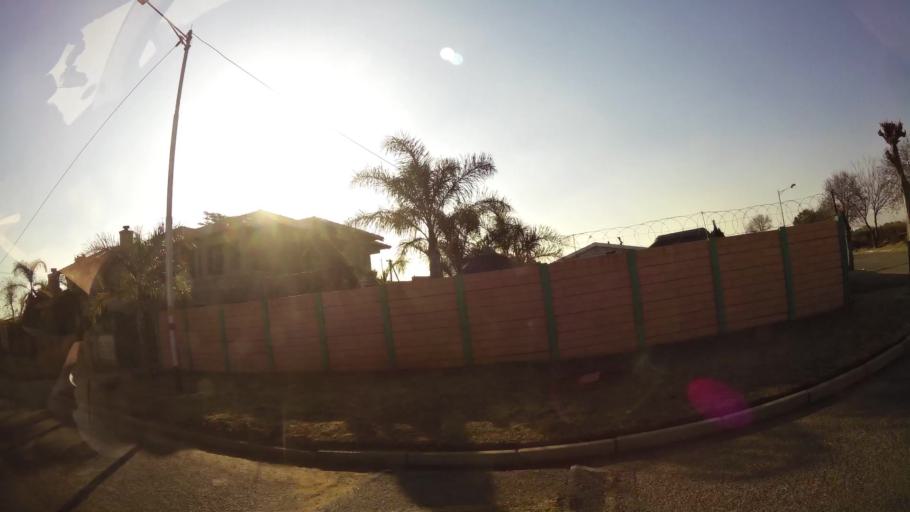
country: ZA
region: Gauteng
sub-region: West Rand District Municipality
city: Randfontein
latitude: -26.1963
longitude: 27.7012
